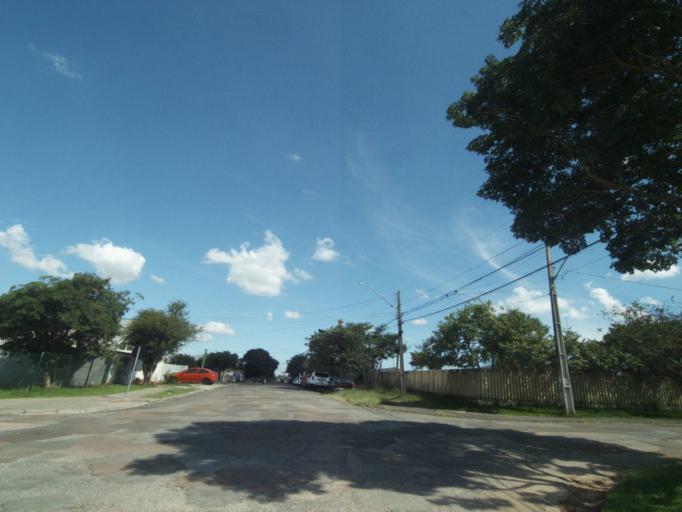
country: BR
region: Parana
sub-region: Pinhais
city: Pinhais
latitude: -25.4612
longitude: -49.2141
